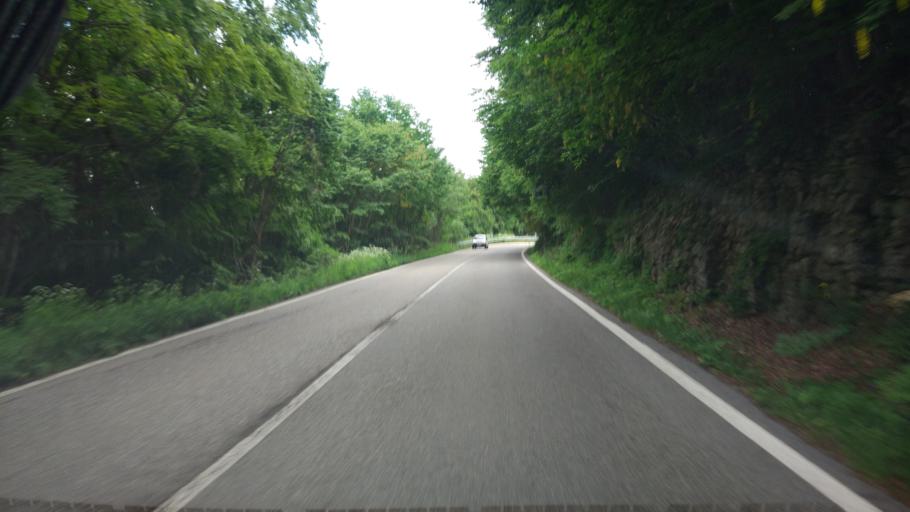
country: IT
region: Veneto
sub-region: Provincia di Verona
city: Bosco Chiesanuova
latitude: 45.6298
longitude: 11.0386
